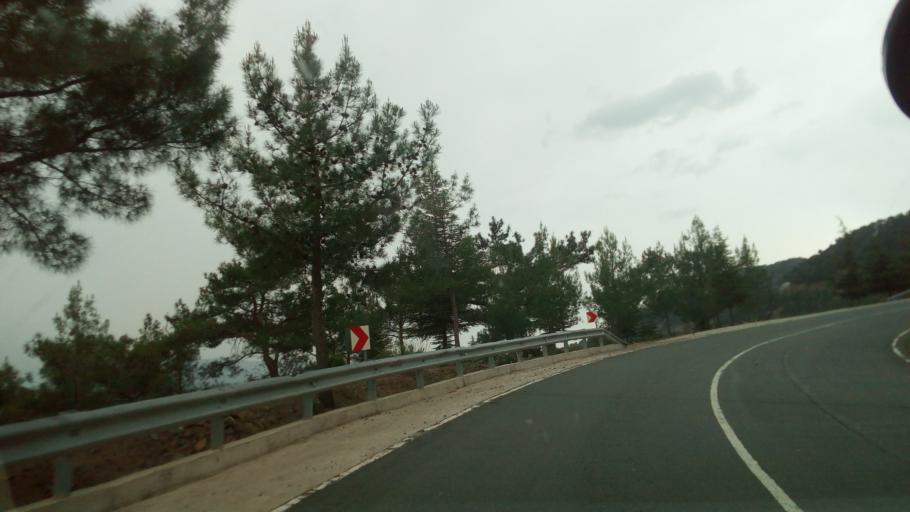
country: CY
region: Lefkosia
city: Lefka
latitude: 35.0000
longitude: 32.7360
